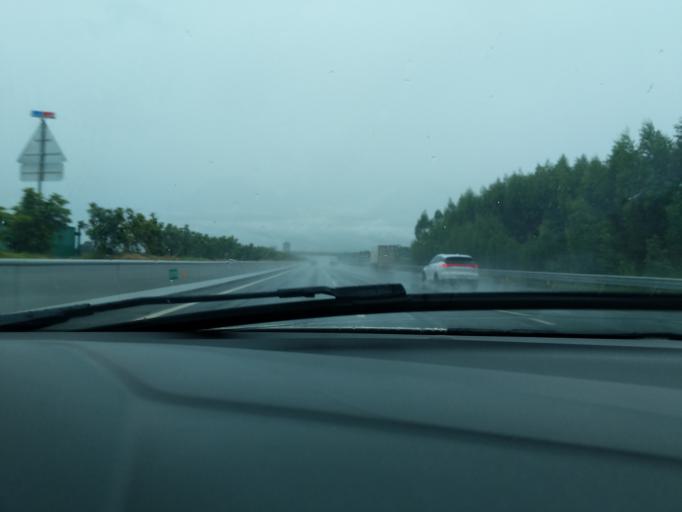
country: CN
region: Guangdong
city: Zhishan
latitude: 22.4845
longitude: 112.7833
